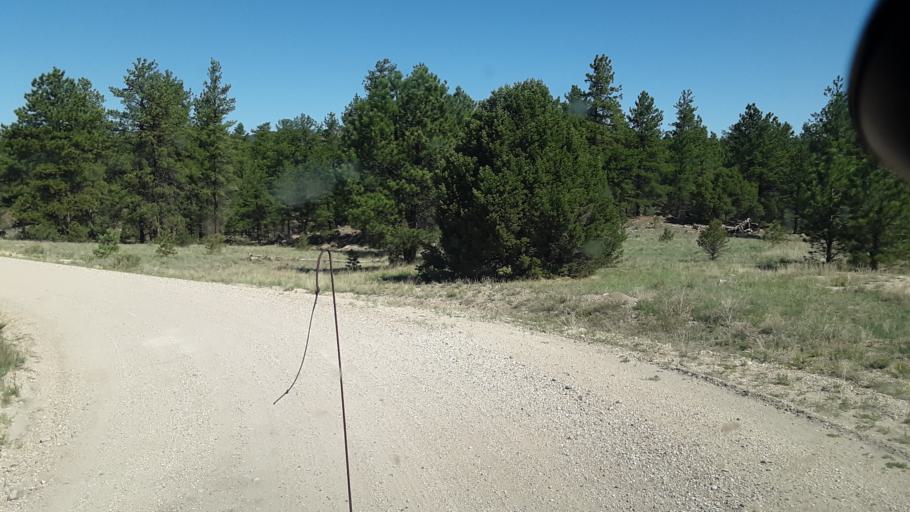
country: US
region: Colorado
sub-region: Custer County
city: Westcliffe
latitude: 38.2919
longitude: -105.4611
